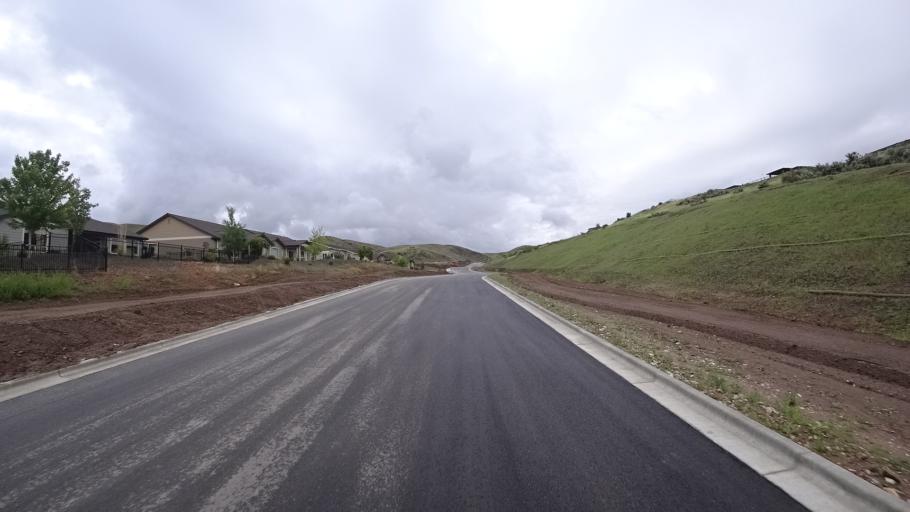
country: US
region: Idaho
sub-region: Ada County
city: Eagle
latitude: 43.7732
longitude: -116.2558
